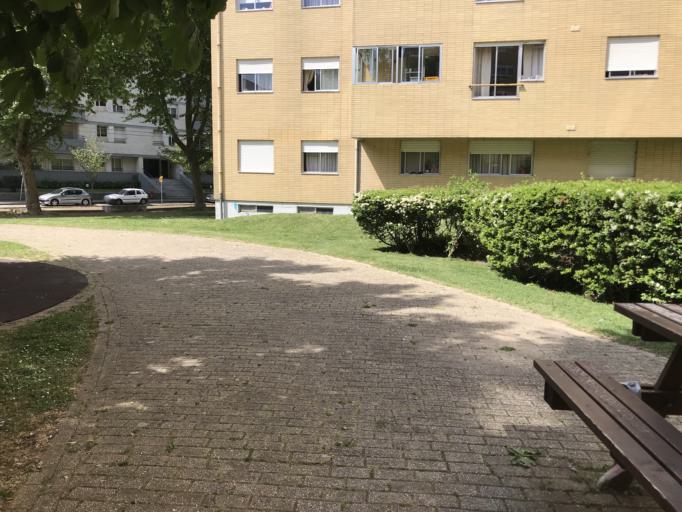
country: PT
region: Porto
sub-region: Matosinhos
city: Senhora da Hora
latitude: 41.1912
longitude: -8.6562
